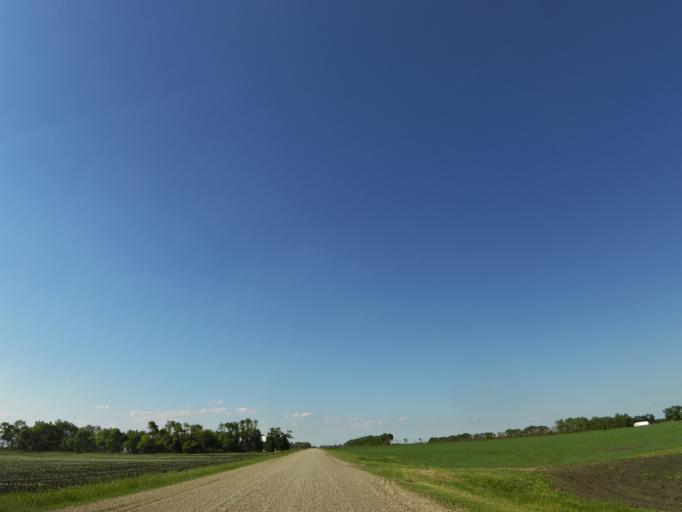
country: US
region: North Dakota
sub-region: Walsh County
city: Grafton
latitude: 48.3494
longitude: -97.2561
